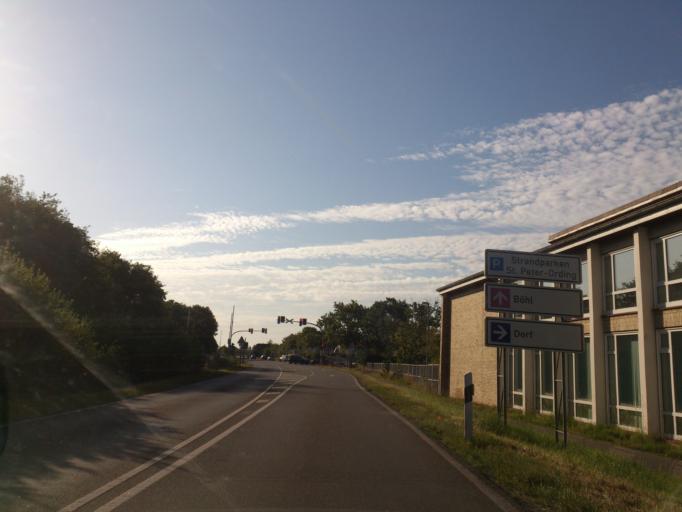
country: DE
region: Schleswig-Holstein
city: Sankt Peter-Ording
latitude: 54.3077
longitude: 8.6345
